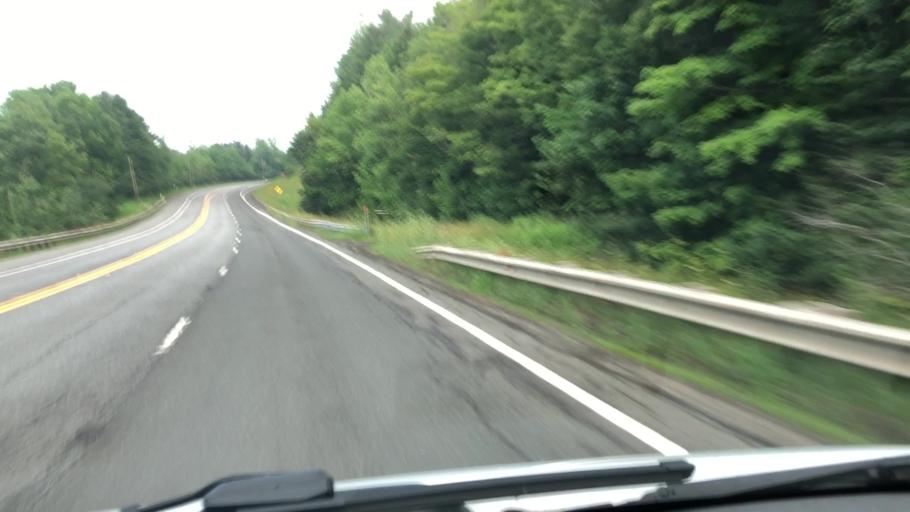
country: US
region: Massachusetts
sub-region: Berkshire County
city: Hinsdale
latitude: 42.4968
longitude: -73.0167
